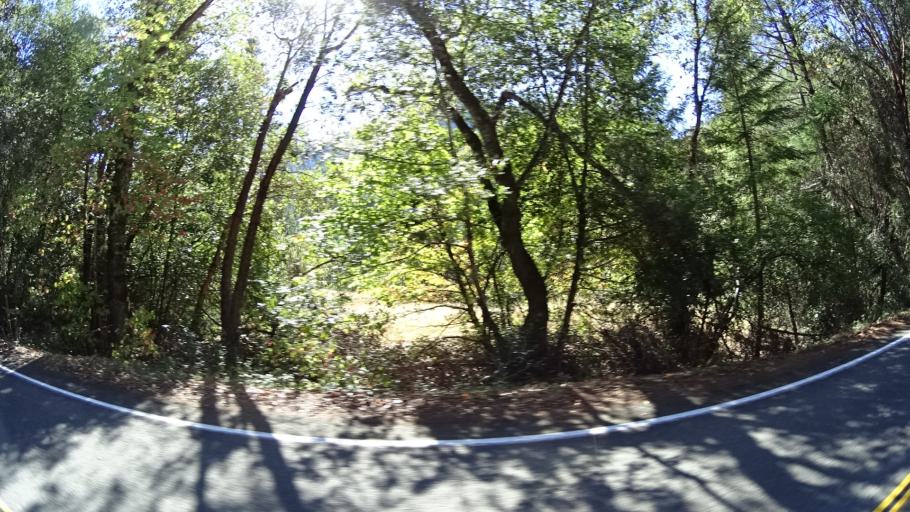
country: US
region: California
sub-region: Siskiyou County
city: Happy Camp
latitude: 41.3754
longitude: -123.4520
